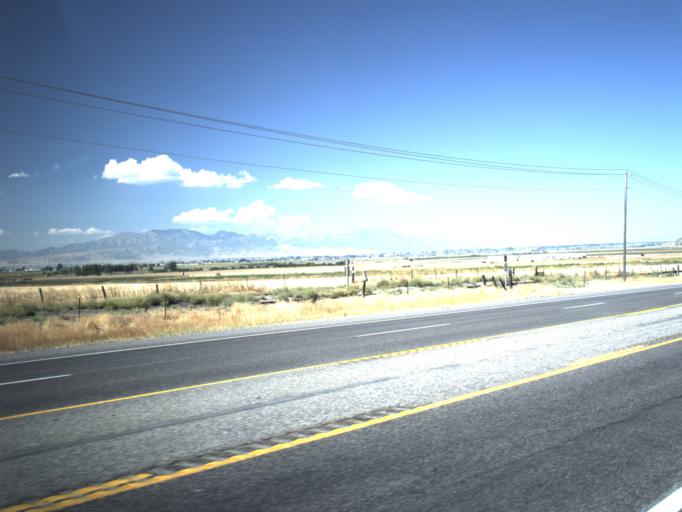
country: US
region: Utah
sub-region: Cache County
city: Richmond
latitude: 41.9664
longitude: -111.8128
